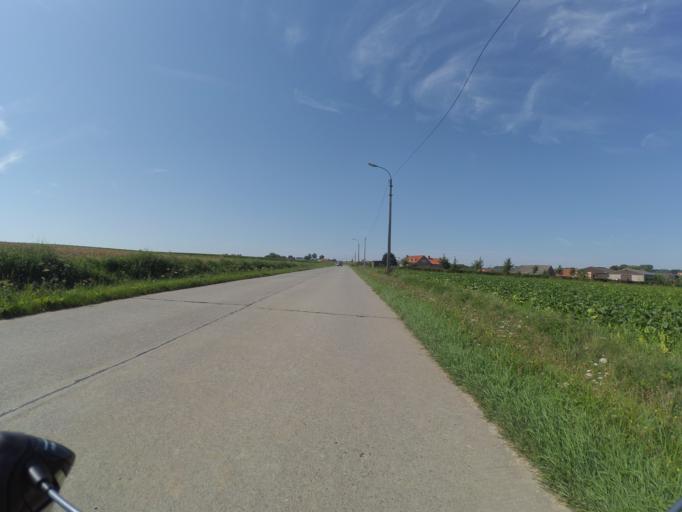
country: BE
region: Flanders
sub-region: Provincie Oost-Vlaanderen
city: Oudenaarde
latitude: 50.8486
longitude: 3.5555
